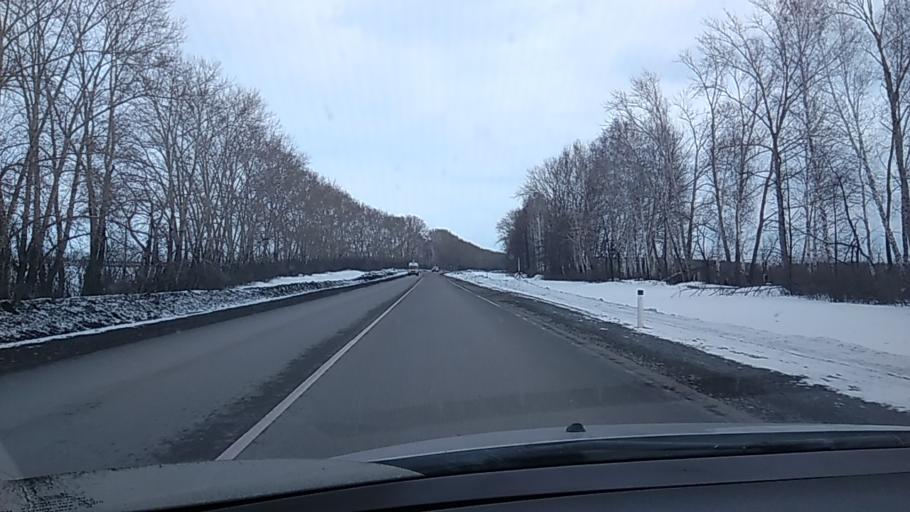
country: RU
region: Sverdlovsk
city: Dvurechensk
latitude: 56.6489
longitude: 61.2034
